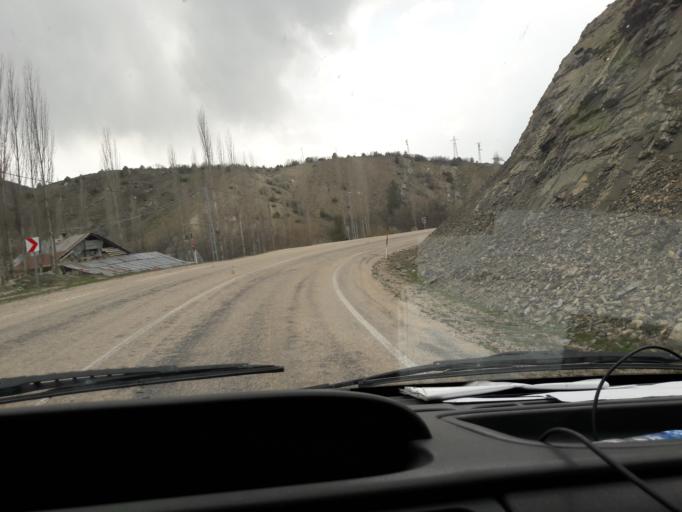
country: TR
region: Giresun
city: Alucra
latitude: 40.2915
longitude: 38.8089
